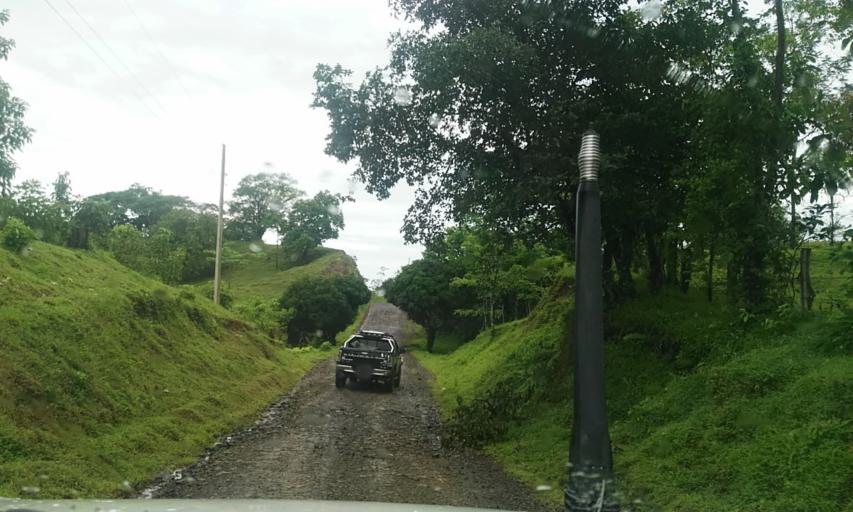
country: NI
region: Matagalpa
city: Rio Blanco
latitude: 12.9979
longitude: -85.1972
